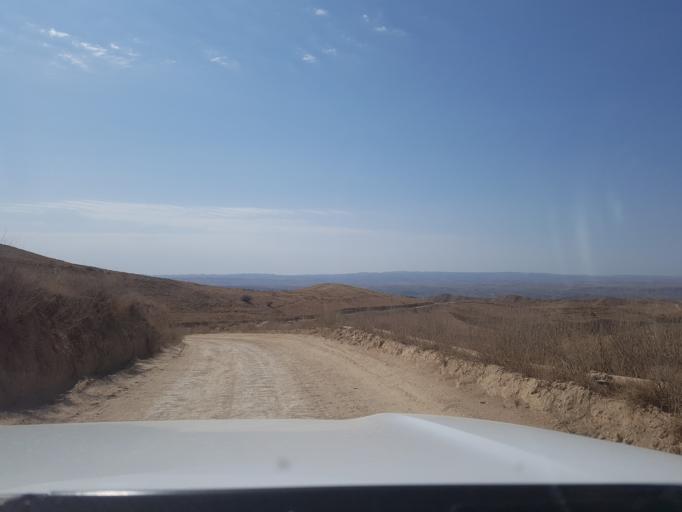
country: TM
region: Ahal
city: Baharly
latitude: 38.2720
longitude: 56.8952
